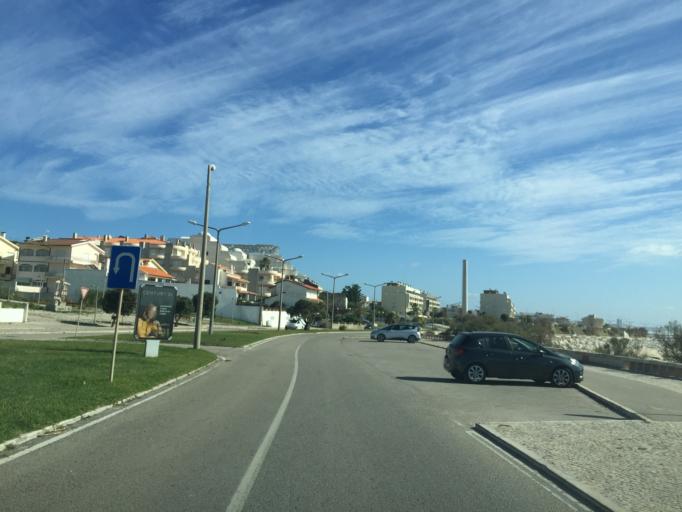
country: PT
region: Coimbra
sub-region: Figueira da Foz
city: Buarcos
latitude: 40.1760
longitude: -8.8974
